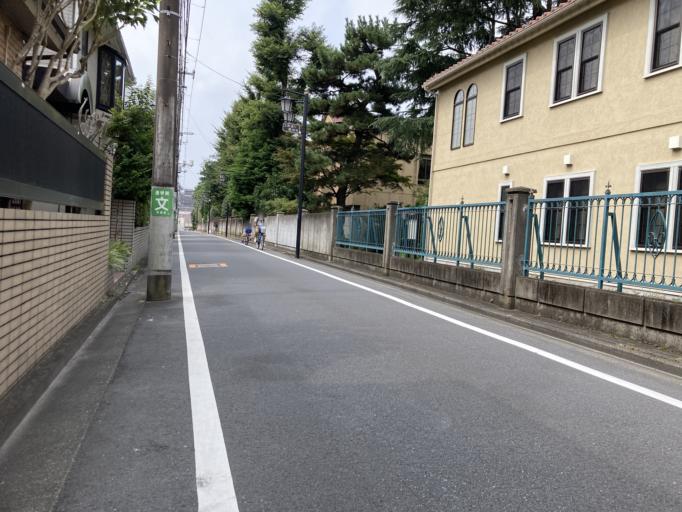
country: JP
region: Tokyo
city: Mitaka-shi
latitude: 35.6942
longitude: 139.5903
